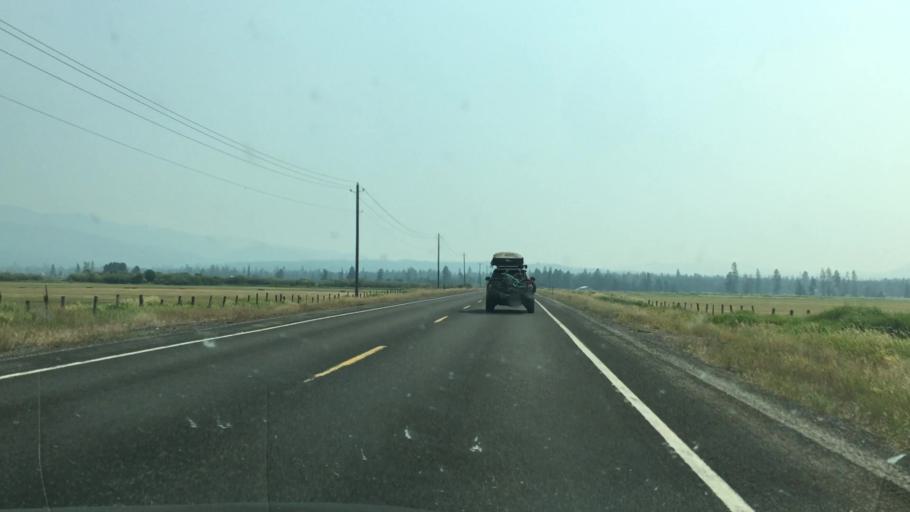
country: US
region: Idaho
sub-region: Valley County
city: Cascade
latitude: 44.4217
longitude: -115.9996
